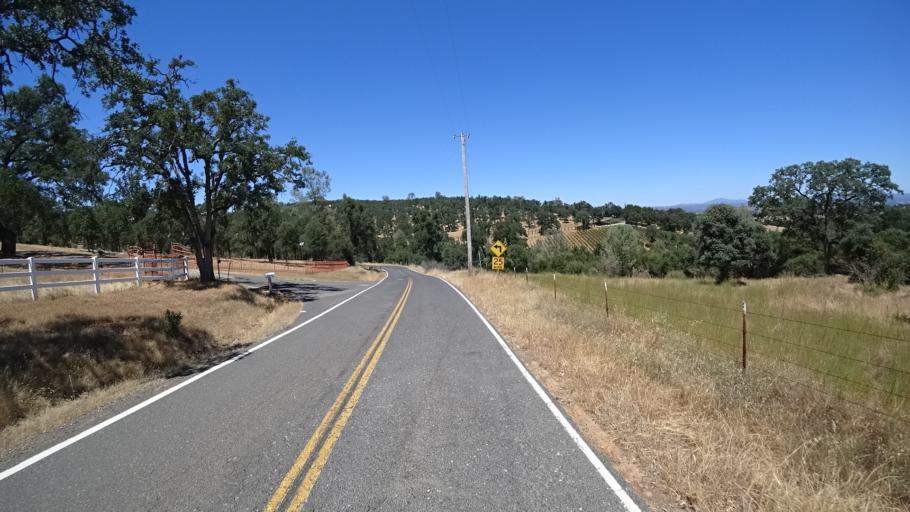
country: US
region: California
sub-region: Calaveras County
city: San Andreas
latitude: 38.0898
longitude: -120.6624
